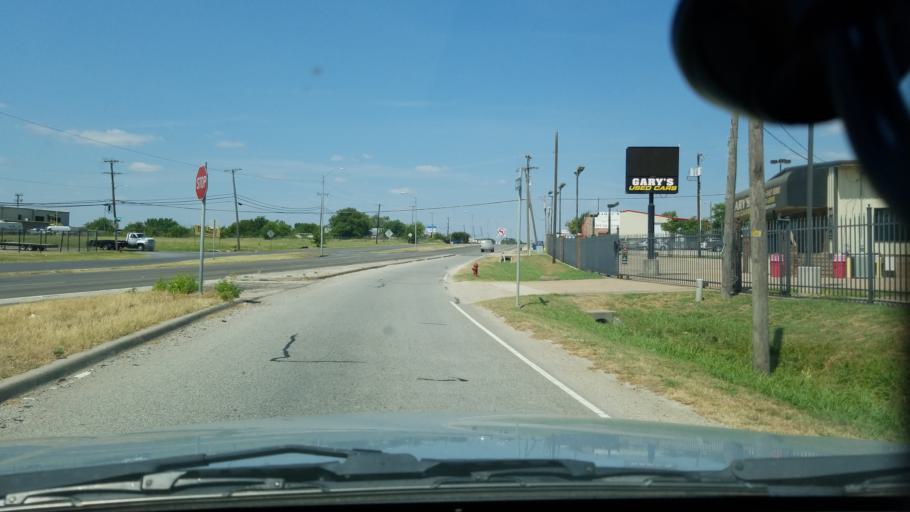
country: US
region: Texas
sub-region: Dallas County
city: Grand Prairie
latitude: 32.7466
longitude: -96.9524
